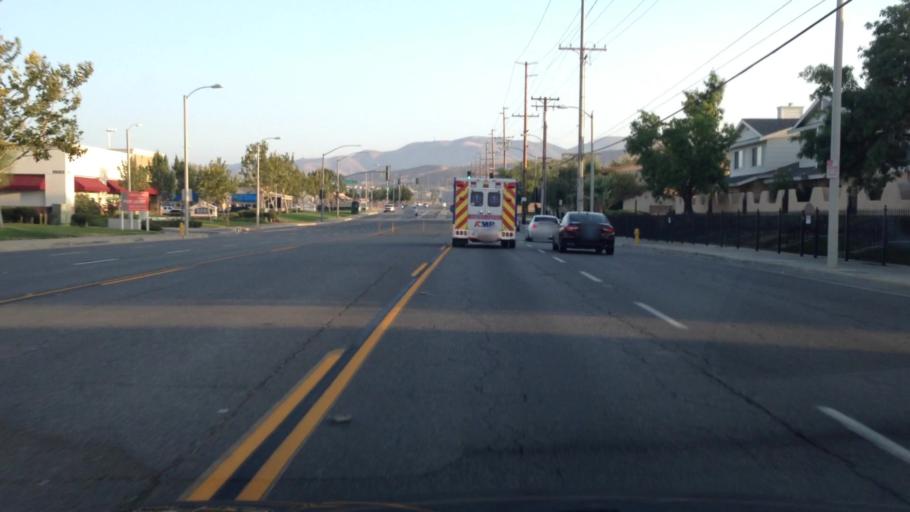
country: US
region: California
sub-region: Los Angeles County
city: Desert View Highlands
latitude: 34.5968
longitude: -118.1477
